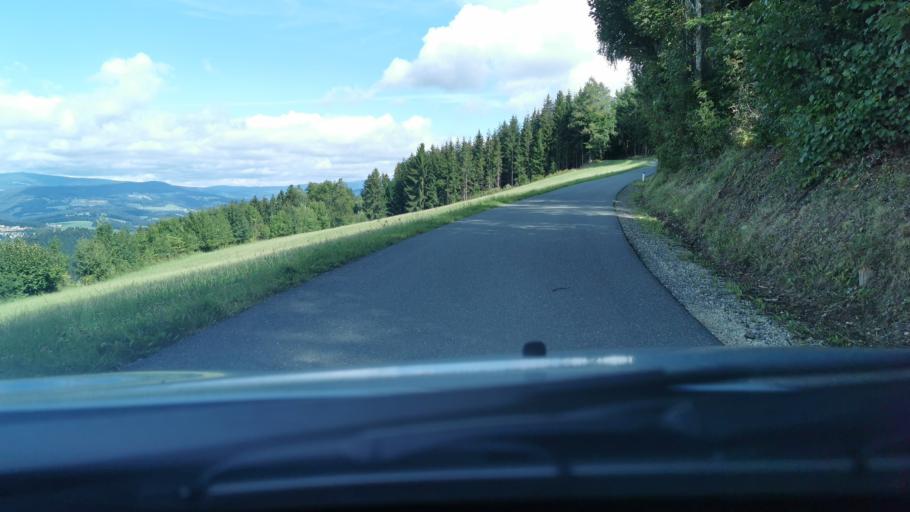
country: AT
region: Styria
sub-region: Politischer Bezirk Weiz
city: Koglhof
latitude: 47.3183
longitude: 15.7063
